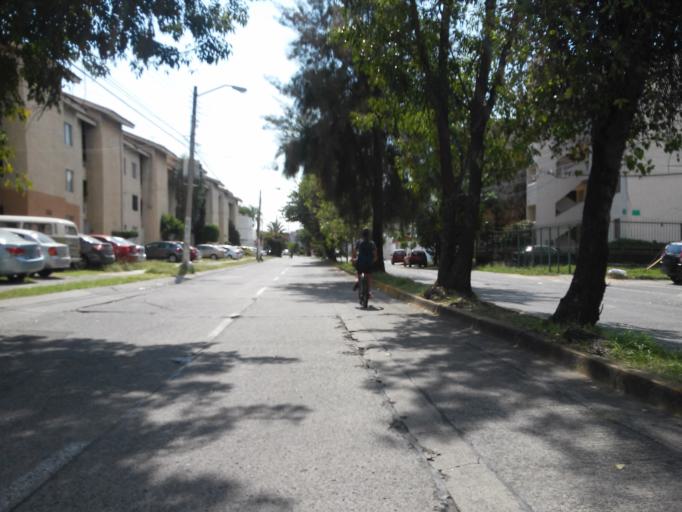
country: MX
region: Jalisco
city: Guadalajara
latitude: 20.6554
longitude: -103.4192
